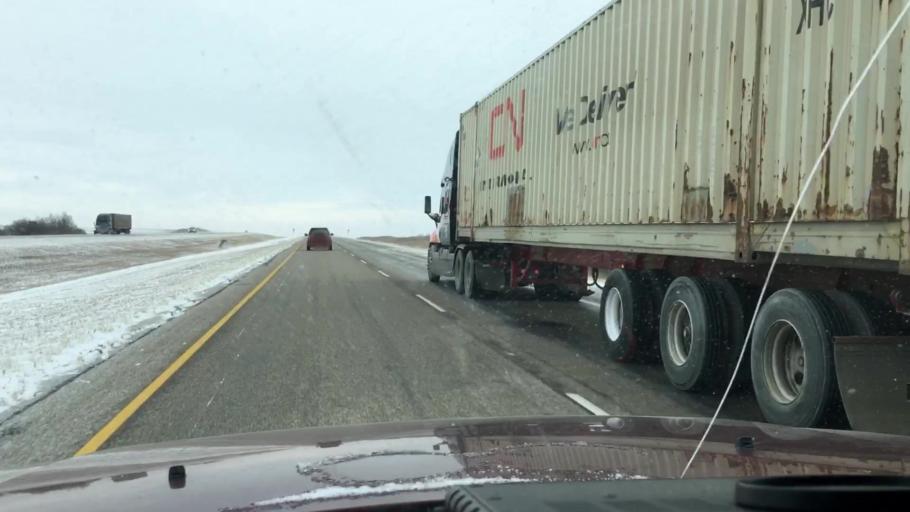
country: CA
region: Saskatchewan
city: Saskatoon
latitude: 51.6735
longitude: -106.4501
